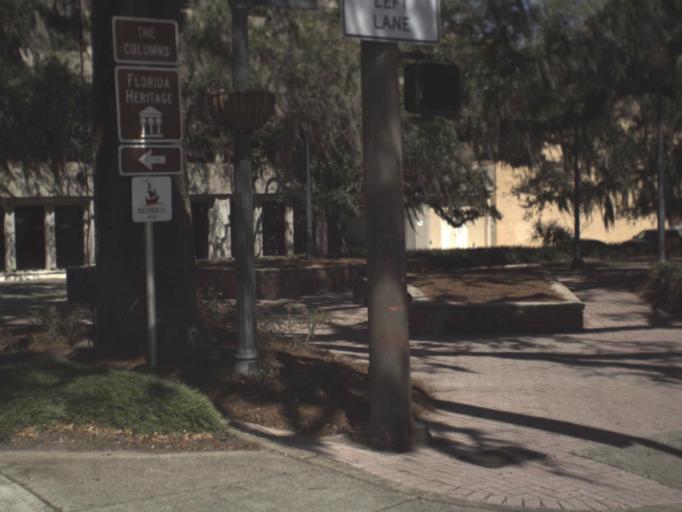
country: US
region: Florida
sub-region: Leon County
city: Tallahassee
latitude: 30.4419
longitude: -84.2806
